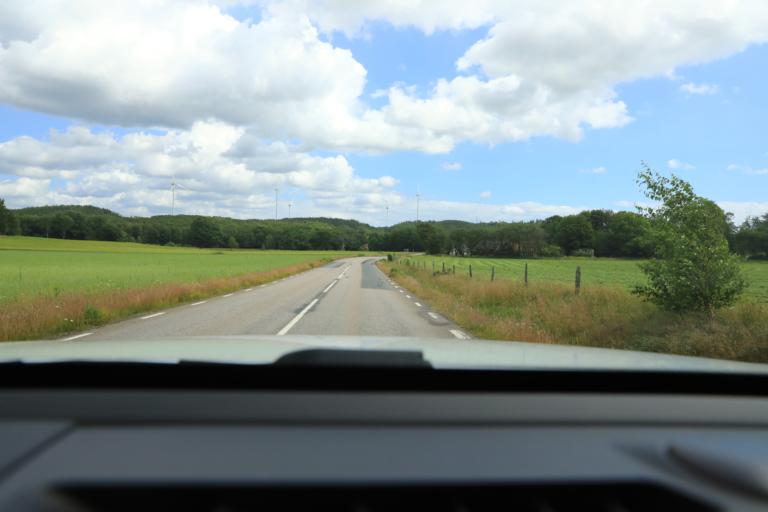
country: SE
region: Halland
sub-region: Varbergs Kommun
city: Tvaaker
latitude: 57.0372
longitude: 12.4673
